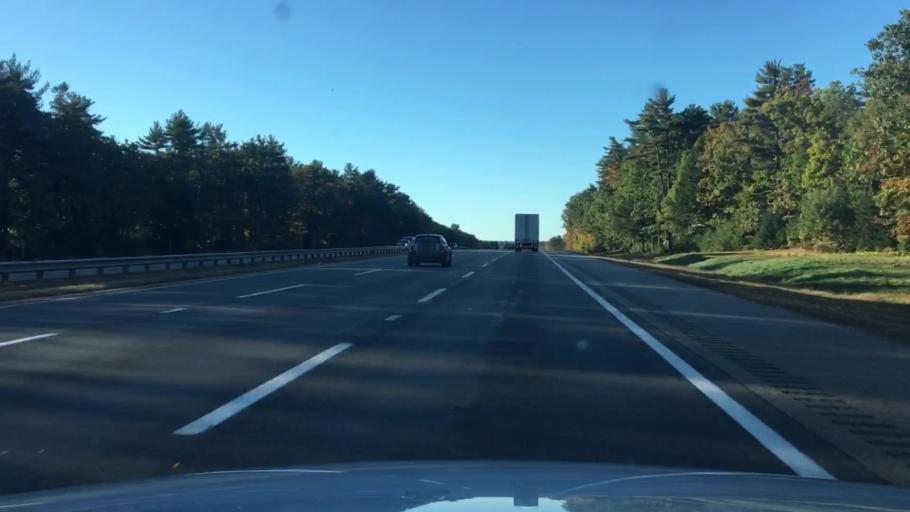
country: US
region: Maine
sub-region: York County
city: Ogunquit
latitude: 43.2796
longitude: -70.6179
